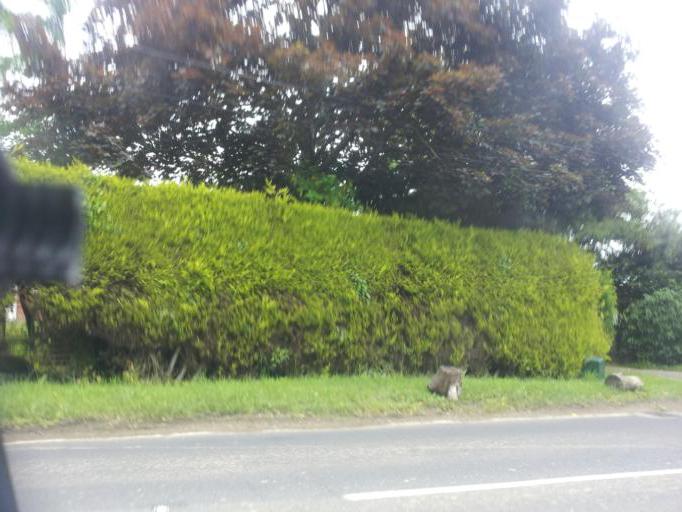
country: GB
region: England
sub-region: Kent
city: Yalding
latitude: 51.2148
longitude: 0.4323
